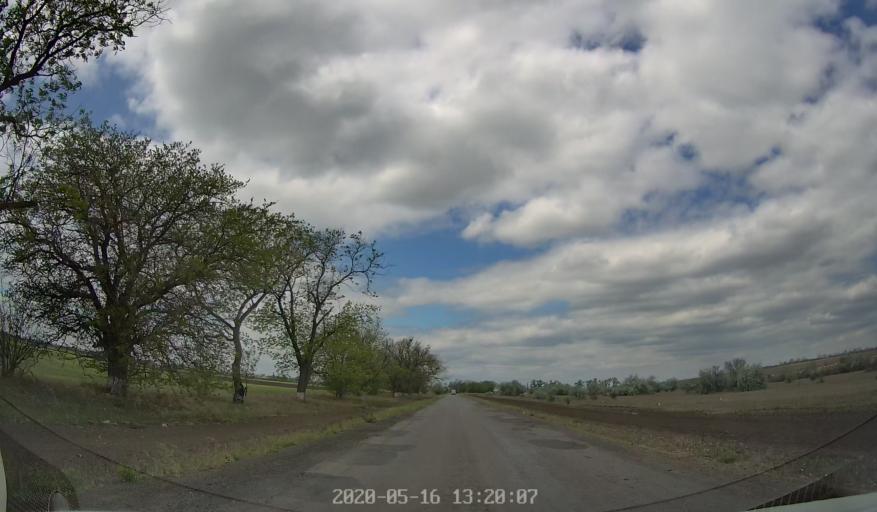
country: UA
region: Odessa
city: Lymanske
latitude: 46.5380
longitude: 30.0523
